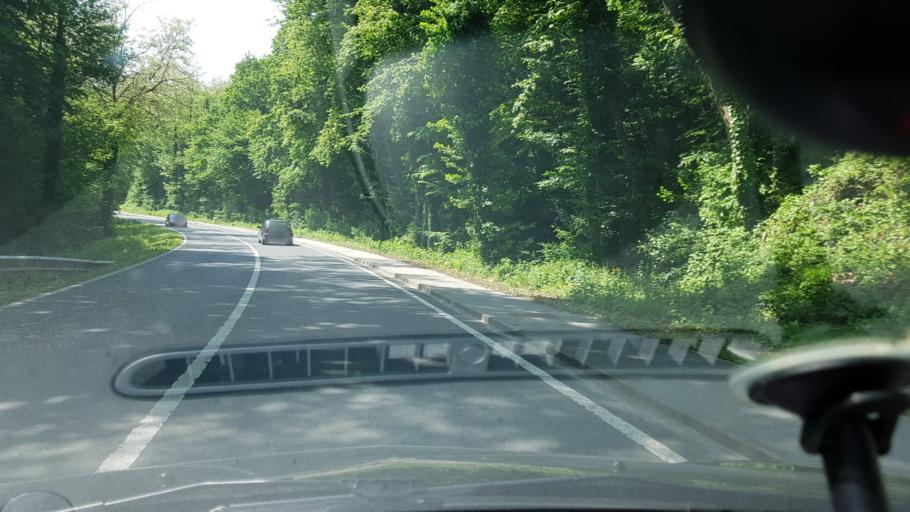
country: HR
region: Krapinsko-Zagorska
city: Marija Bistrica
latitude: 45.9888
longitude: 16.1162
